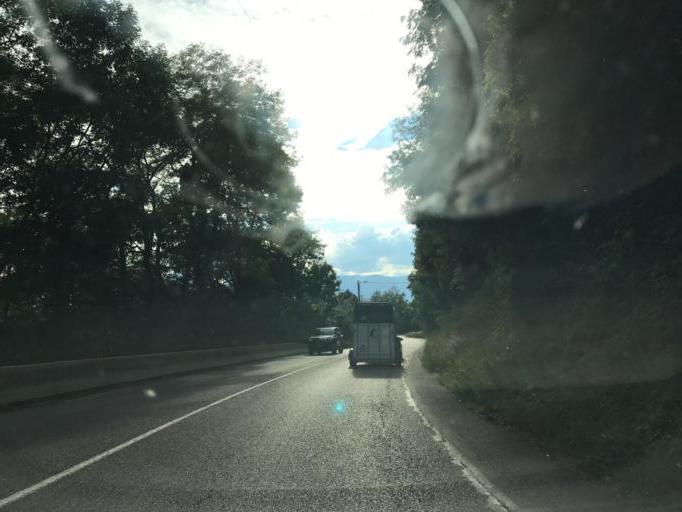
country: FR
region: Rhone-Alpes
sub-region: Departement de l'Ain
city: Bellegarde-sur-Valserine
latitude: 46.0919
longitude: 5.8713
